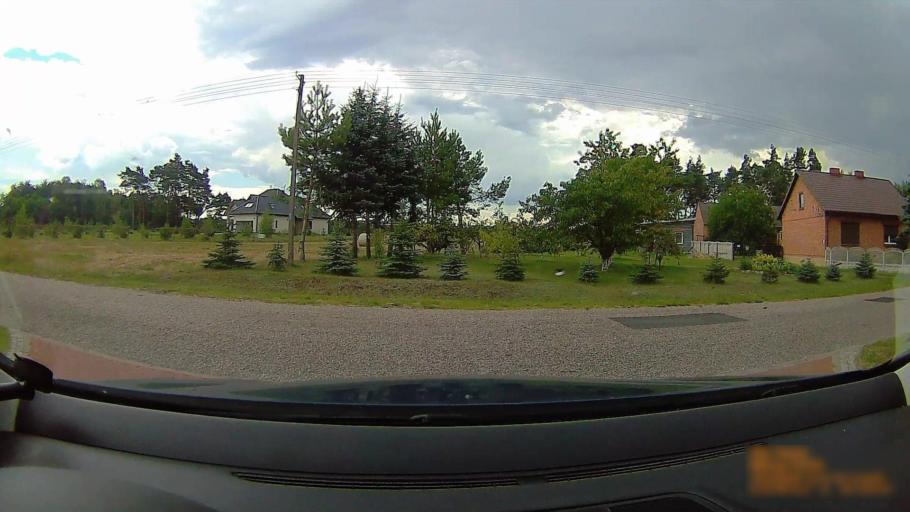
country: PL
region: Greater Poland Voivodeship
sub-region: Powiat koninski
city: Rychwal
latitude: 52.1040
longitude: 18.2061
